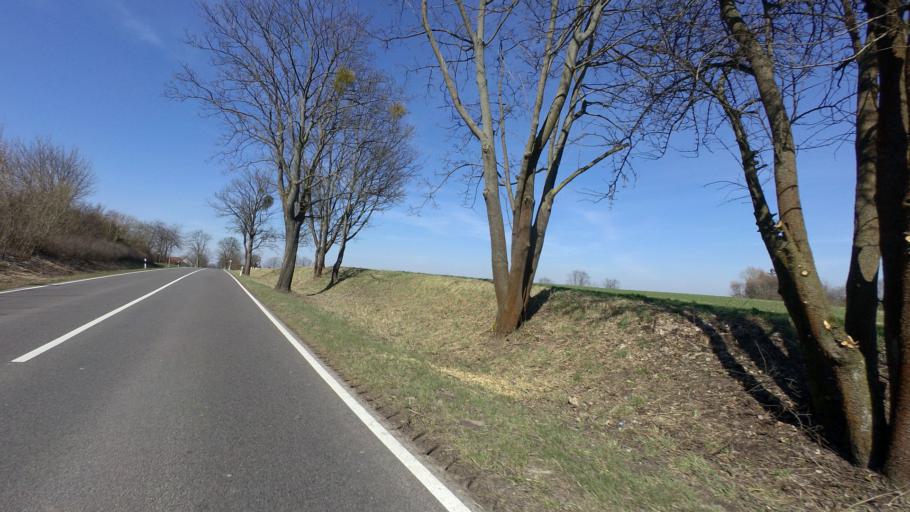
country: DE
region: Brandenburg
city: Protzel
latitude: 52.5975
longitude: 14.0255
